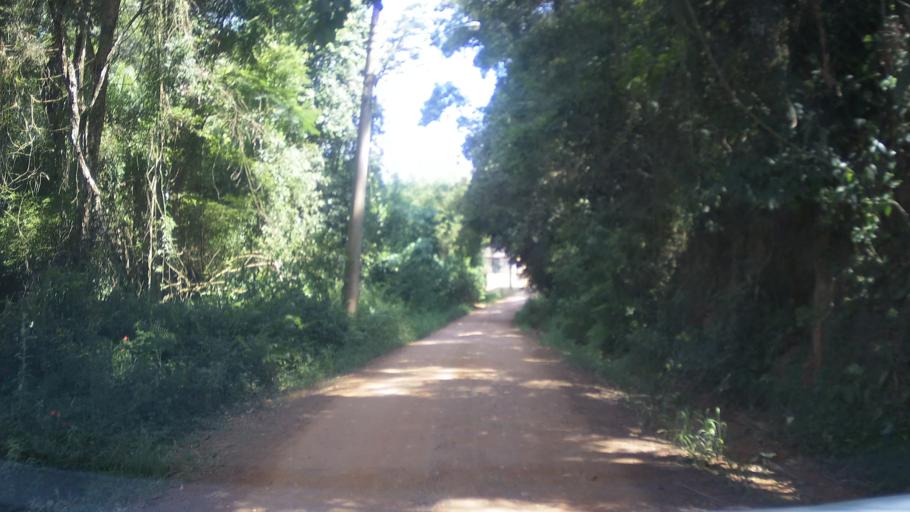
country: BR
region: Sao Paulo
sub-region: Jarinu
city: Jarinu
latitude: -23.1162
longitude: -46.8095
